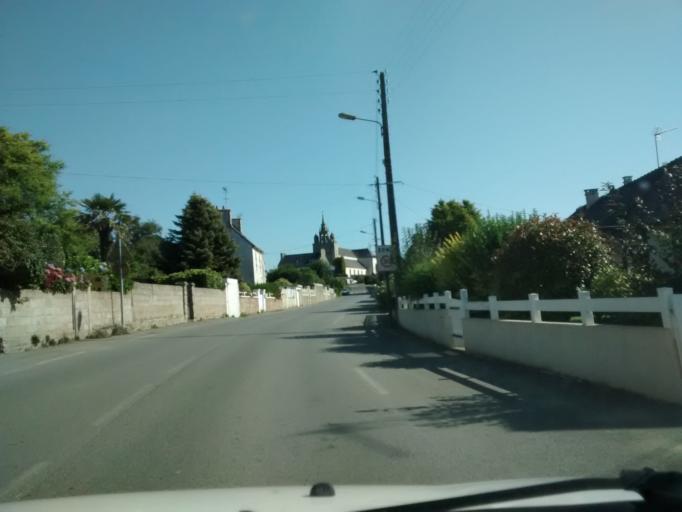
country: FR
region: Brittany
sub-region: Departement des Cotes-d'Armor
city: Tredarzec
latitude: 48.7859
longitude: -3.2017
